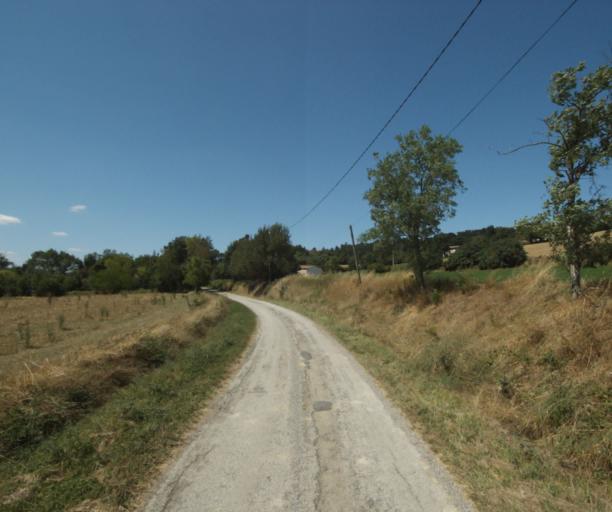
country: FR
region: Midi-Pyrenees
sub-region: Departement de la Haute-Garonne
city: Auriac-sur-Vendinelle
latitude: 43.5013
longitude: 1.8615
